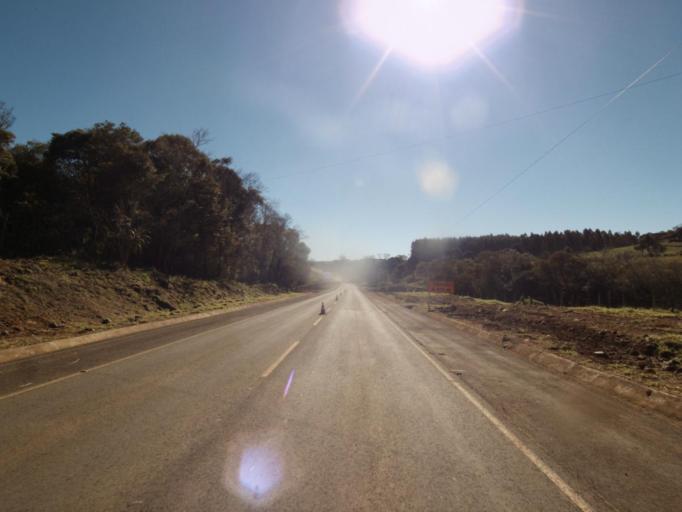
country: AR
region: Misiones
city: Bernardo de Irigoyen
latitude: -26.6329
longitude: -53.6382
